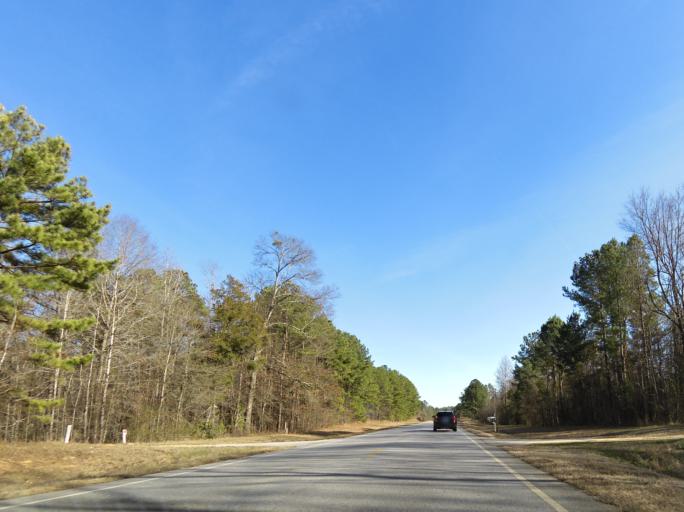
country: US
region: Georgia
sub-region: Crawford County
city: Roberta
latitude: 32.7456
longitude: -84.0720
